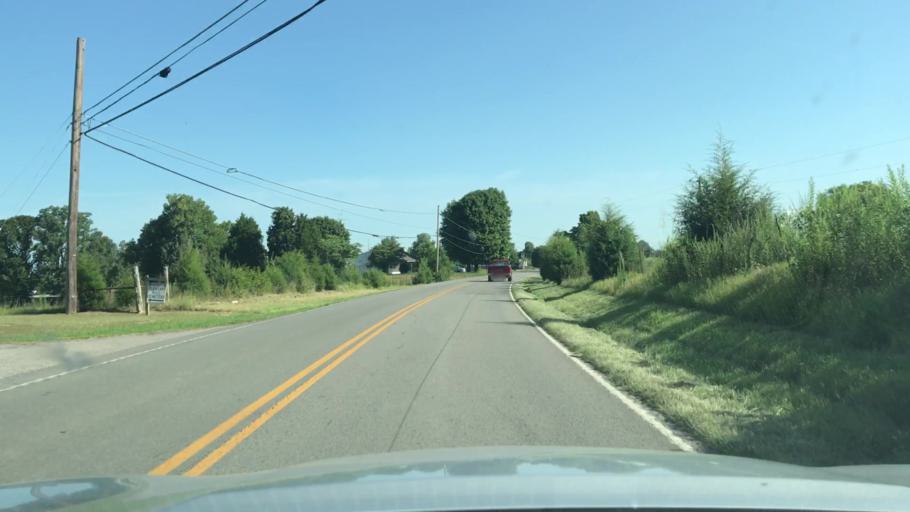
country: US
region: Kentucky
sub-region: Muhlenberg County
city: Greenville
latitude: 37.1743
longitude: -87.1528
